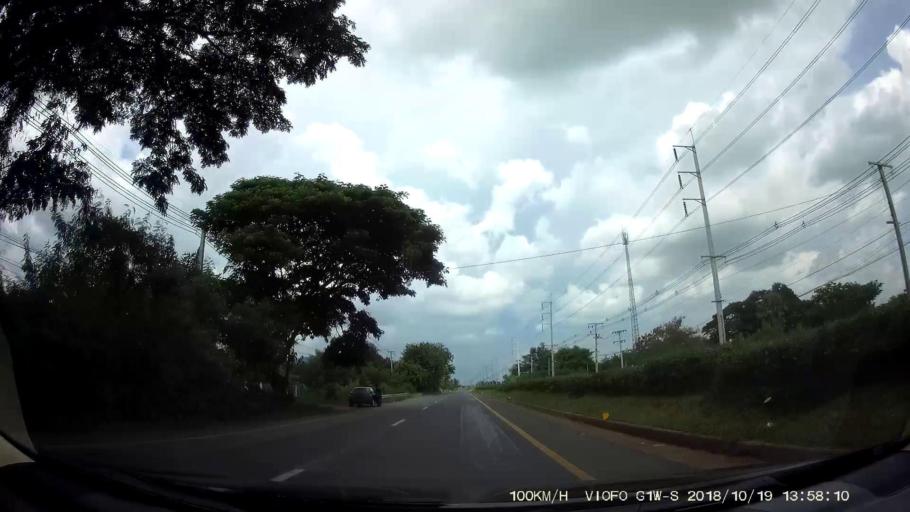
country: TH
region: Chaiyaphum
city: Chaiyaphum
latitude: 15.7951
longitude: 102.0502
